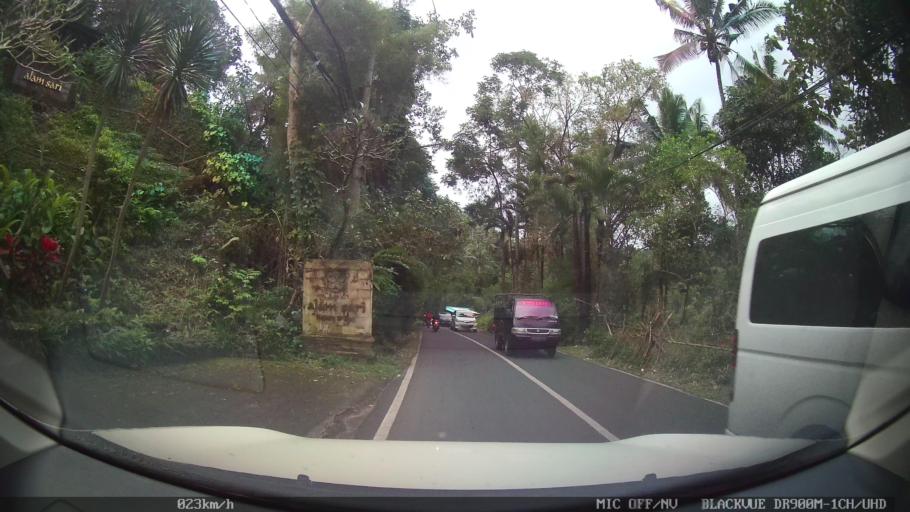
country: ID
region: Bali
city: Banjar Triwangsakeliki
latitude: -8.4479
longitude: 115.2693
